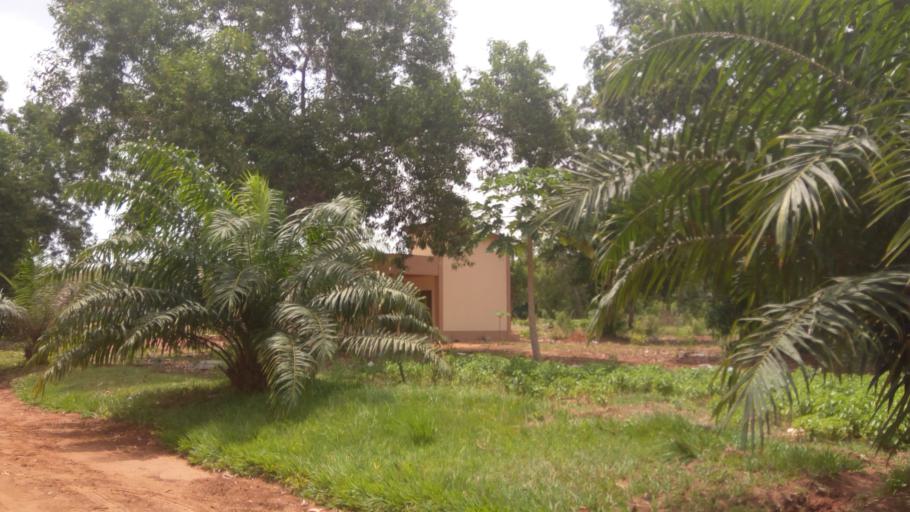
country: BJ
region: Atlantique
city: Abomey-Calavi
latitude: 6.4142
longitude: 2.3387
